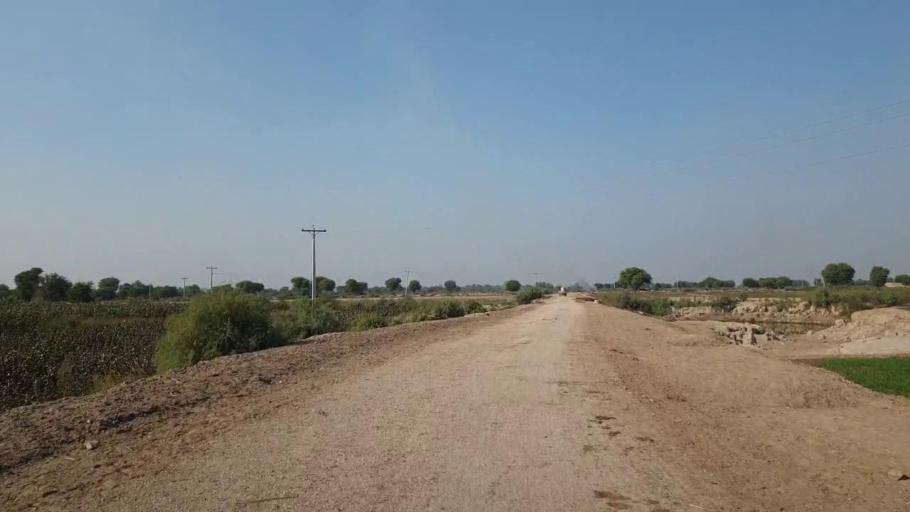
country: PK
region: Sindh
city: Sehwan
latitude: 26.4517
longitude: 67.8163
